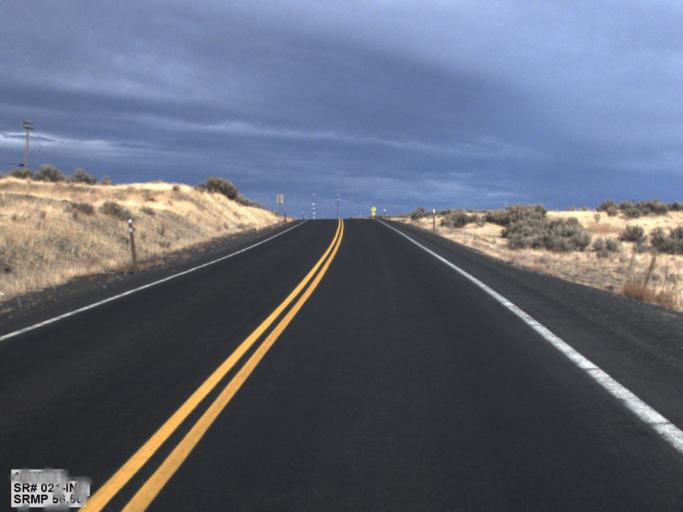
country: US
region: Washington
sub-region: Adams County
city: Ritzville
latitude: 47.3407
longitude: -118.6889
